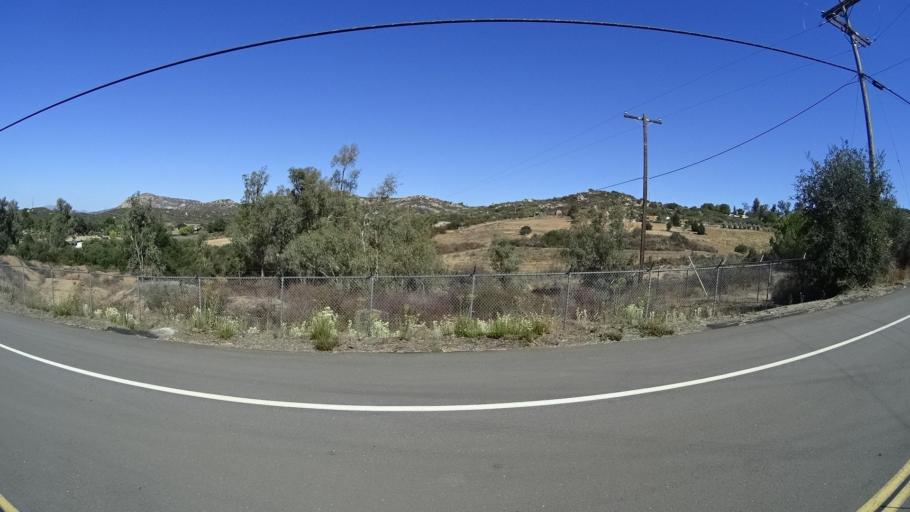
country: US
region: California
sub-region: San Diego County
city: Descanso
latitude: 32.7645
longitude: -116.6787
